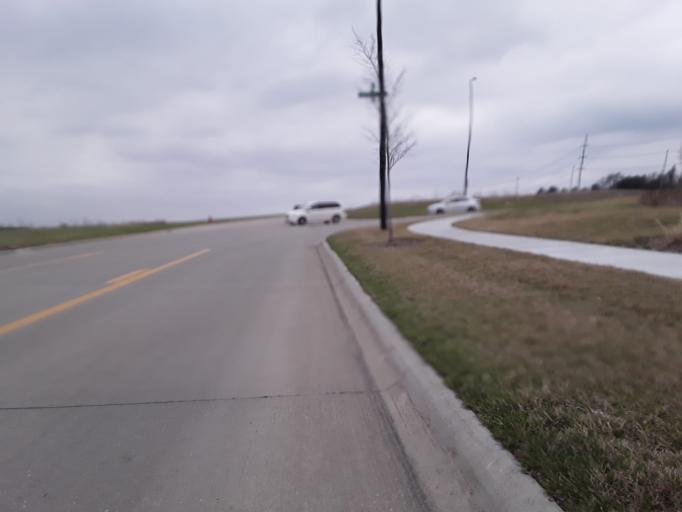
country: US
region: Nebraska
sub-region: Lancaster County
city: Lincoln
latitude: 40.8467
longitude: -96.6041
